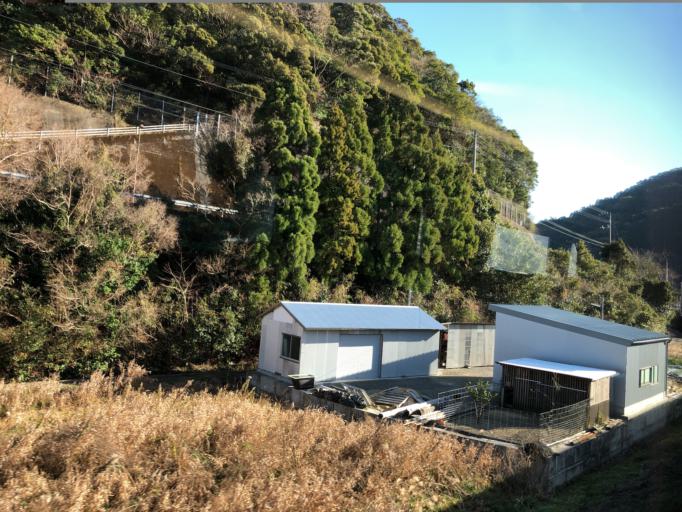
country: JP
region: Kochi
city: Nakamura
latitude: 33.0828
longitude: 133.1018
